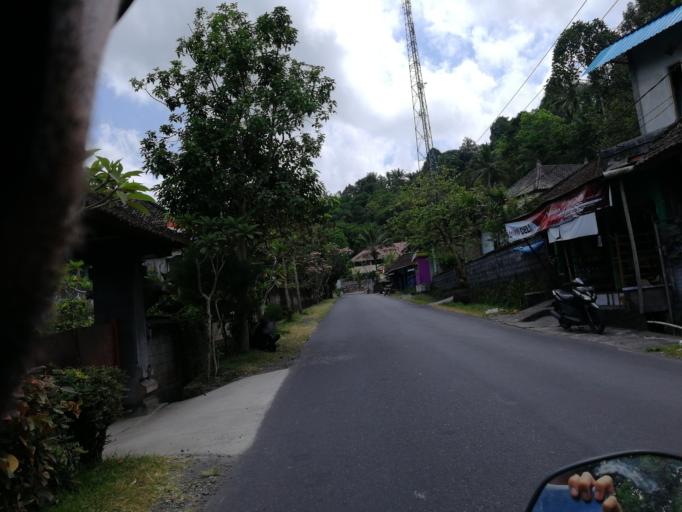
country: ID
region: Bali
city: Banjar Wangsian
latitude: -8.4557
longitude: 115.4518
